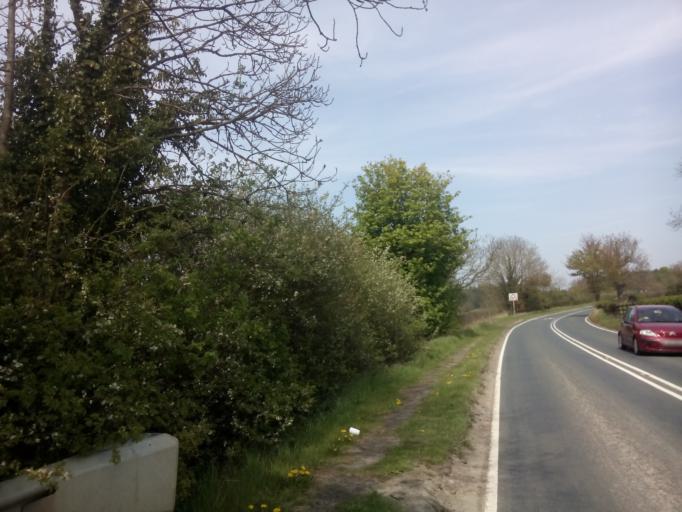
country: GB
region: England
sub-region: County Durham
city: West Rainton
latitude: 54.7925
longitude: -1.5136
